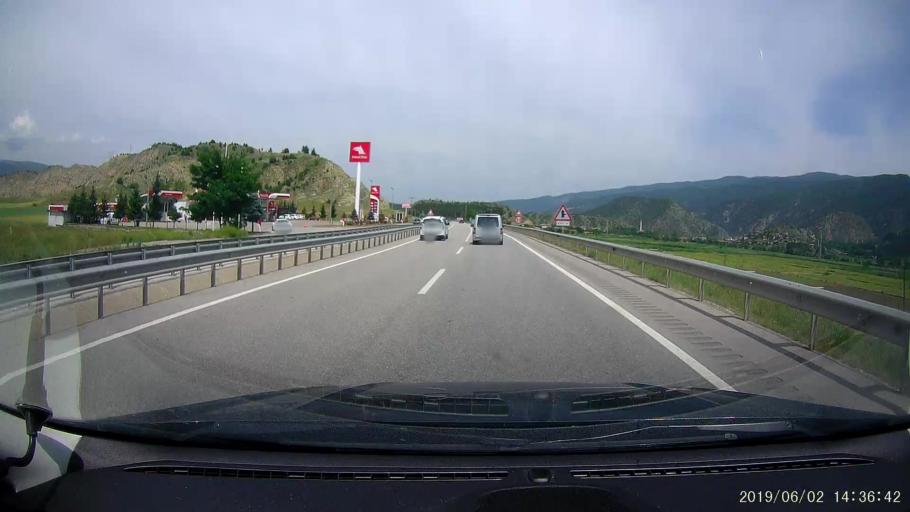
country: TR
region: Kastamonu
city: Tosya
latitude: 41.0479
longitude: 34.2417
